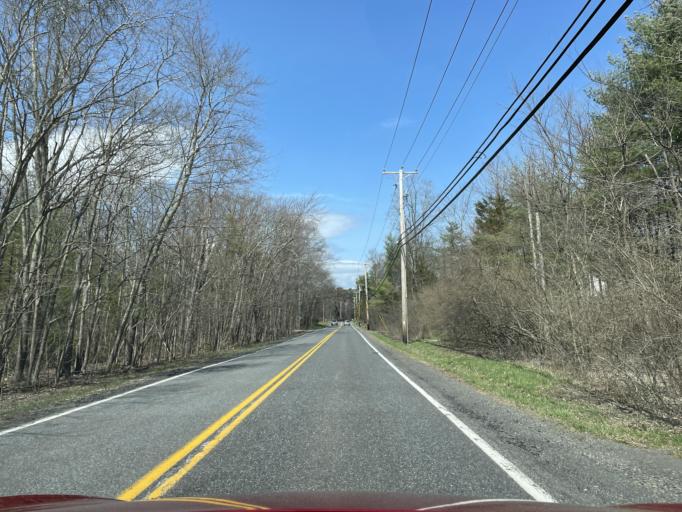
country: US
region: New York
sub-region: Ulster County
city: Manorville
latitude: 42.0946
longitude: -74.0182
